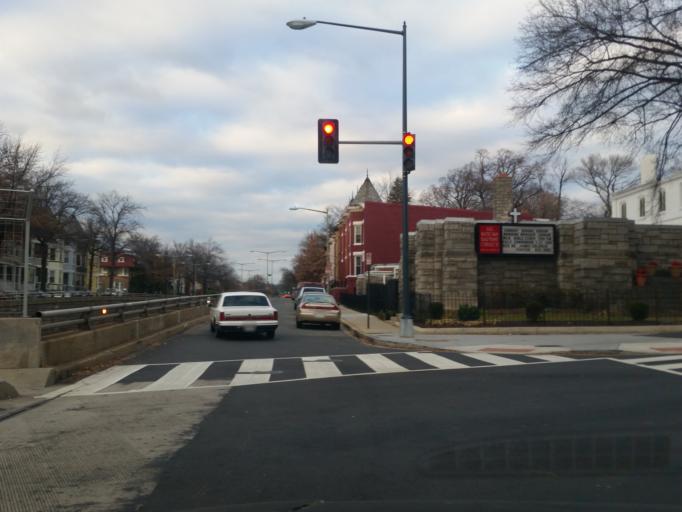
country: US
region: Washington, D.C.
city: Washington, D.C.
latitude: 38.9169
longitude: -77.0090
